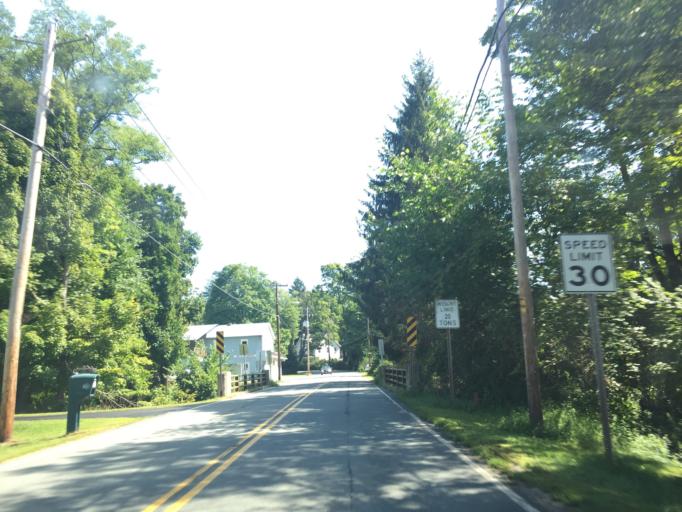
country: US
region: New York
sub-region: Sullivan County
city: Livingston Manor
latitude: 41.8043
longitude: -74.9950
